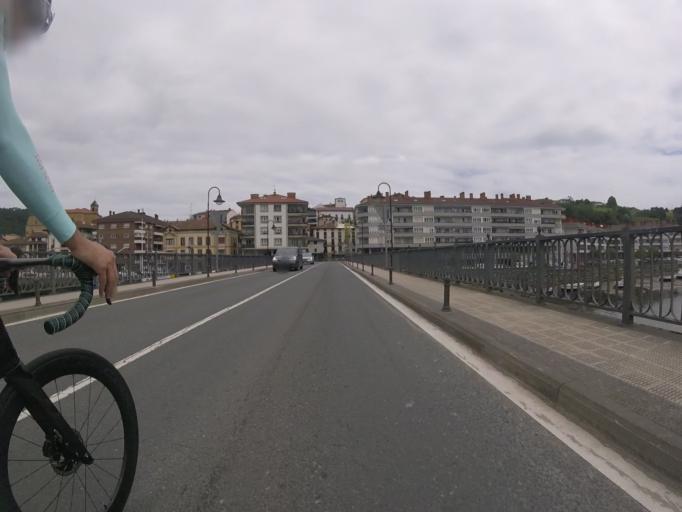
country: ES
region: Basque Country
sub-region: Provincia de Guipuzcoa
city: Orio
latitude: 43.2755
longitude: -2.1256
